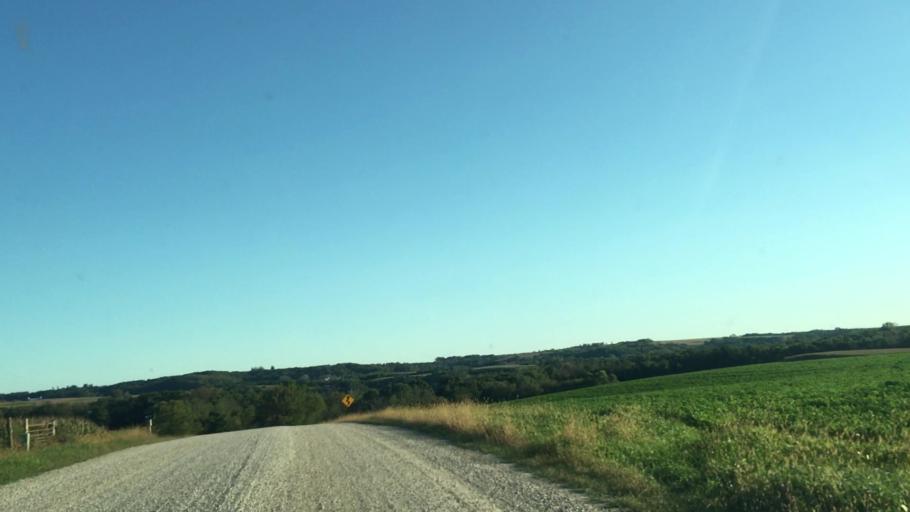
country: US
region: Minnesota
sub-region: Fillmore County
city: Preston
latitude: 43.7680
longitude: -92.0294
